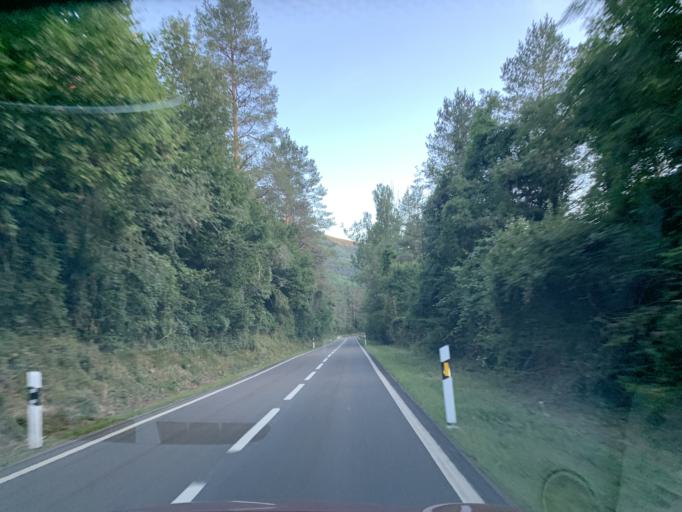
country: ES
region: Aragon
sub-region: Provincia de Huesca
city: Broto
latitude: 42.5614
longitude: -0.1166
